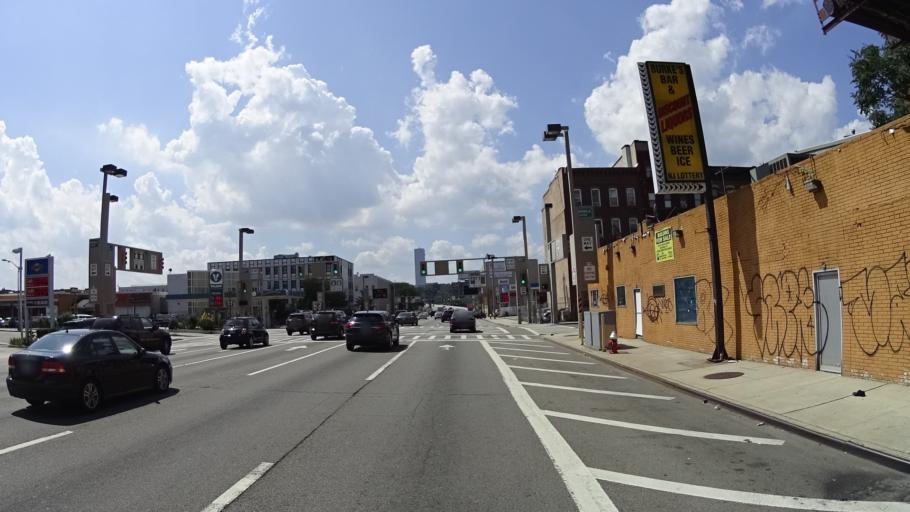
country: US
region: New Jersey
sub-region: Hudson County
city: Hoboken
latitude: 40.7317
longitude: -74.0405
